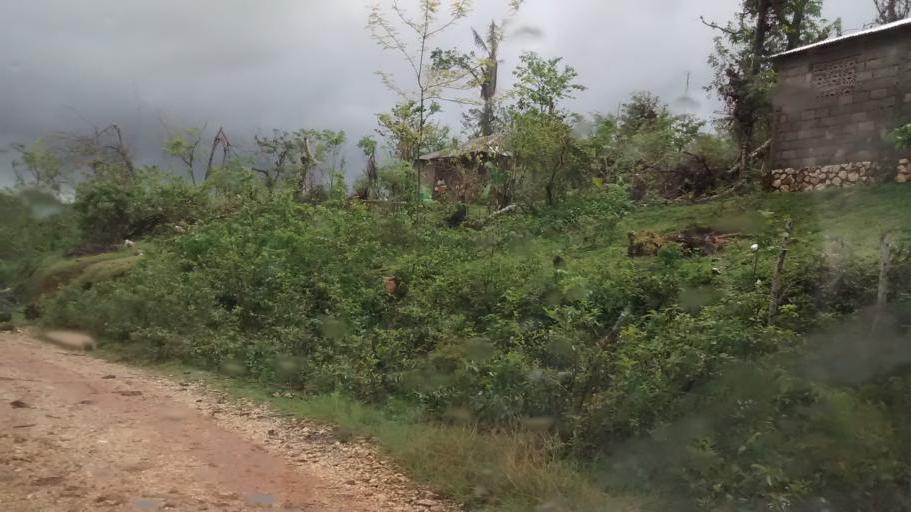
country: HT
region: Grandans
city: Corail
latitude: 18.5367
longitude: -73.9880
